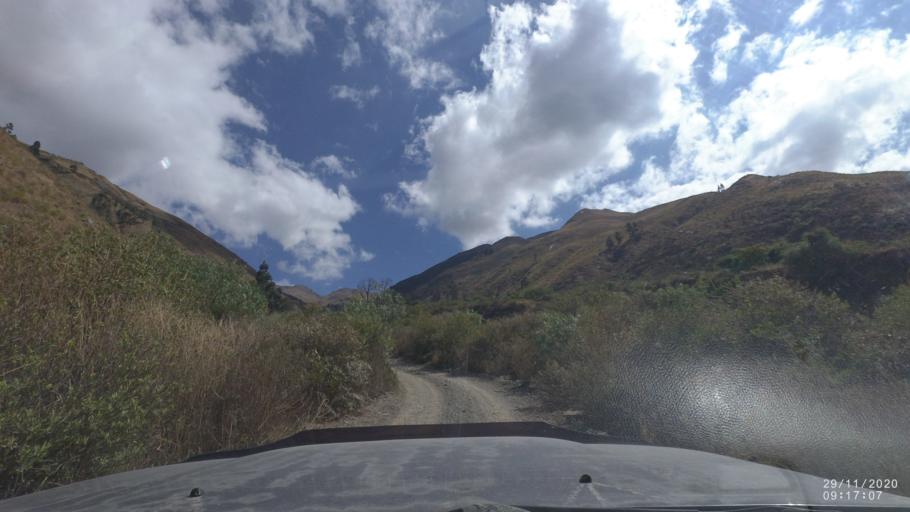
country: BO
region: Cochabamba
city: Cochabamba
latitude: -17.3253
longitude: -66.1845
